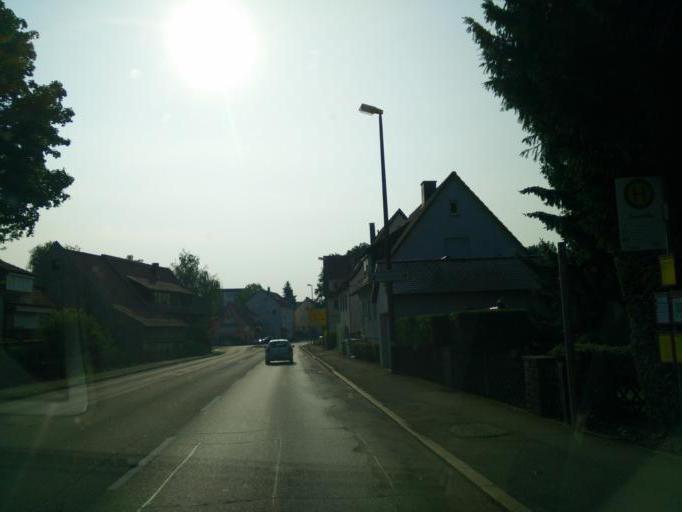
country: DE
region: Baden-Wuerttemberg
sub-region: Tuebingen Region
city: Tuebingen
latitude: 48.5289
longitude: 9.0762
